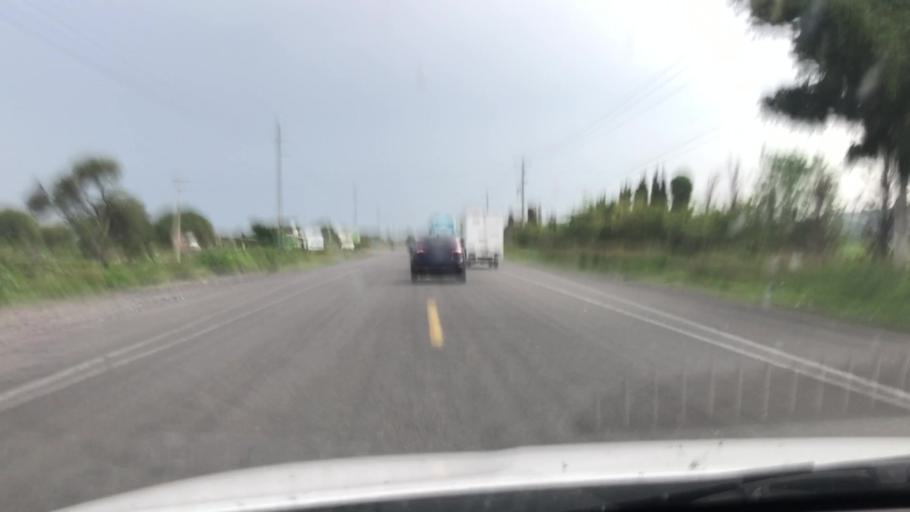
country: MX
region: Michoacan
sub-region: Vista Hermosa
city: Los Pilares
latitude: 20.2769
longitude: -102.3855
